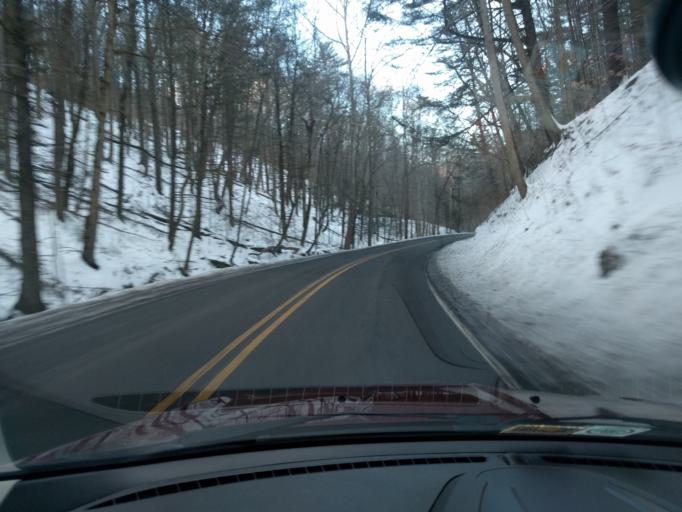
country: US
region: Virginia
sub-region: Bath County
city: Warm Springs
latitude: 38.0755
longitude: -79.8722
